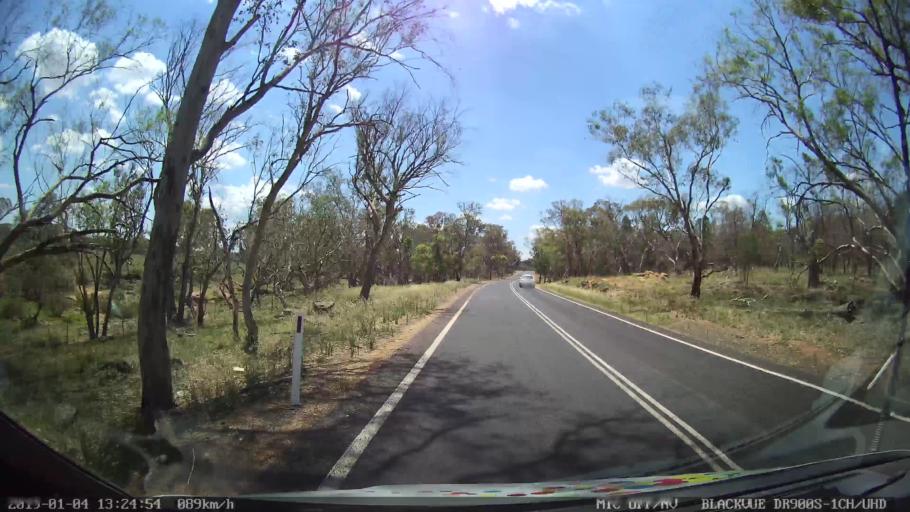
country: AU
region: New South Wales
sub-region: Parkes
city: Peak Hill
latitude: -32.6997
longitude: 148.5538
